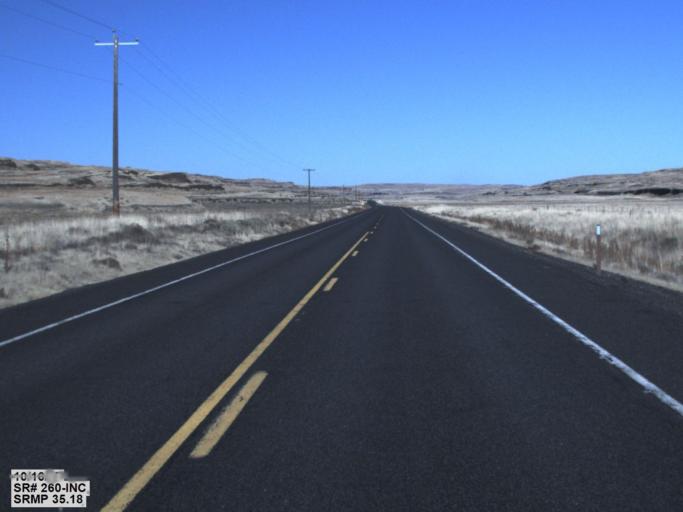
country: US
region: Washington
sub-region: Adams County
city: Ritzville
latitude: 46.7197
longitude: -118.3771
